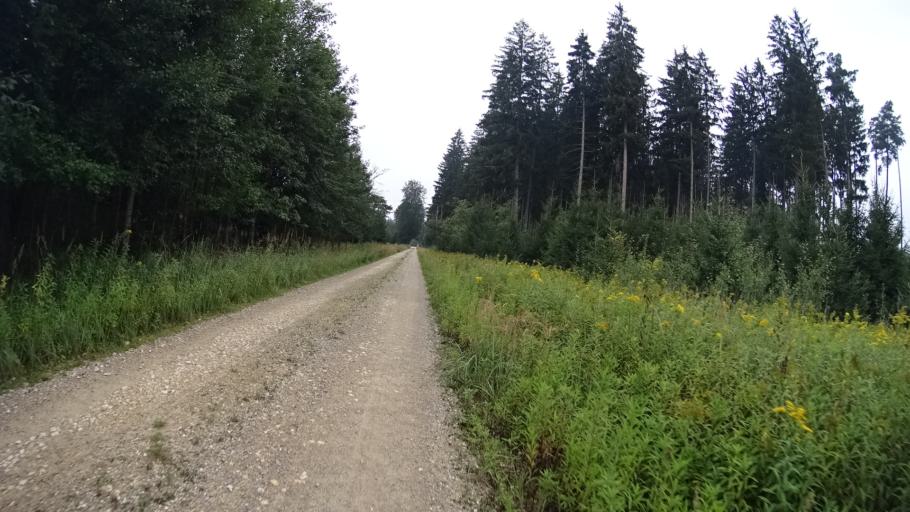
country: DE
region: Bavaria
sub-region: Upper Bavaria
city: Stammham
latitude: 48.8989
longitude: 11.4987
